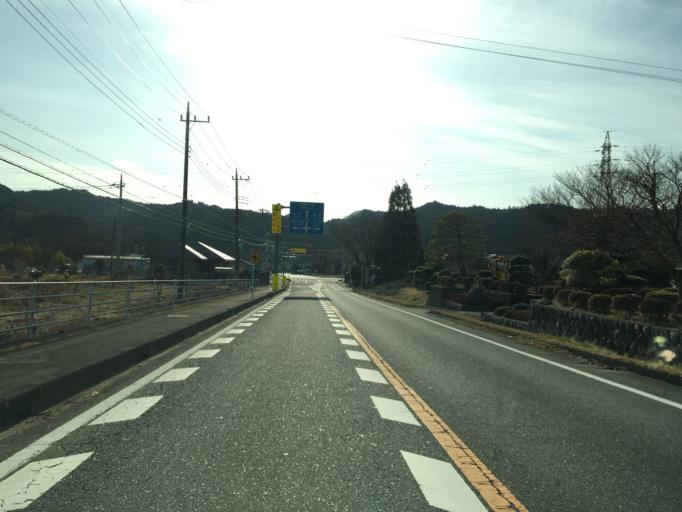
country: JP
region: Ibaraki
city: Daigo
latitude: 36.7166
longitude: 140.5016
